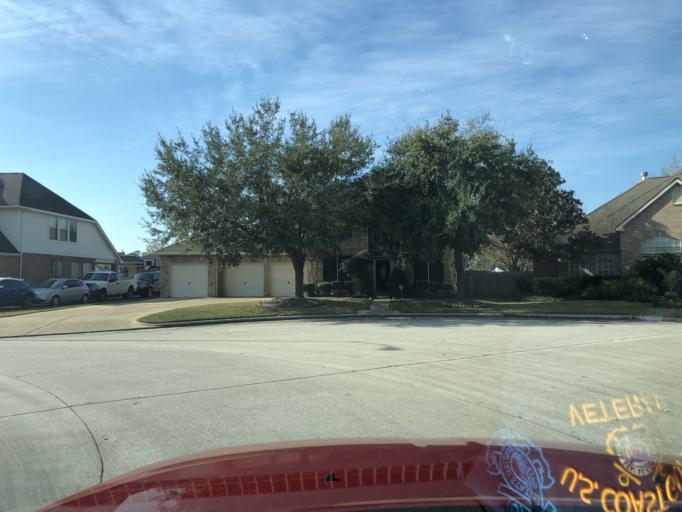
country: US
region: Texas
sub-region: Harris County
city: Tomball
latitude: 30.0275
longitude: -95.5609
